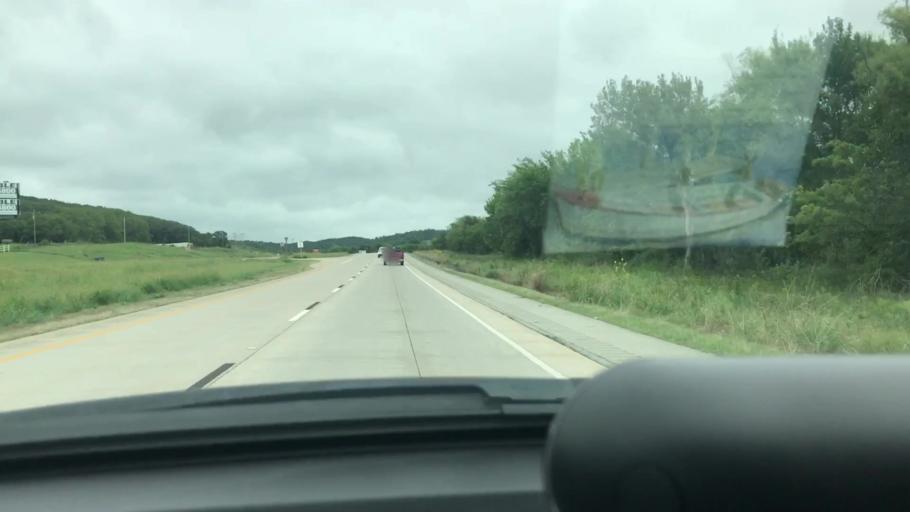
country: US
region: Oklahoma
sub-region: Atoka County
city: Atoka
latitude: 34.4320
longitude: -96.0806
